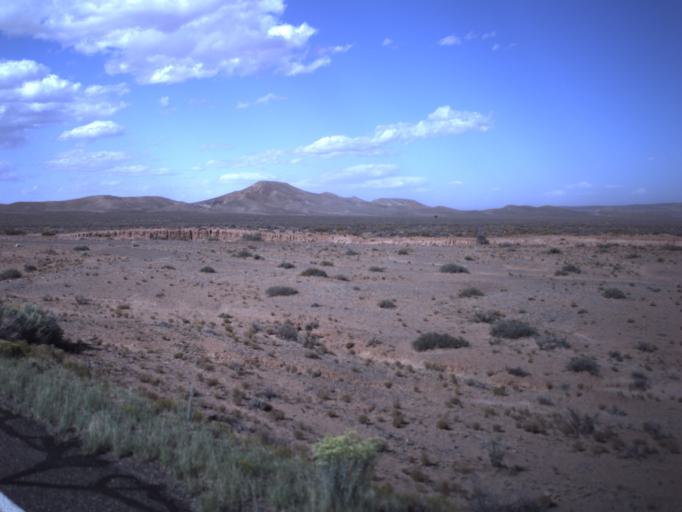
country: US
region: Utah
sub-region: Wayne County
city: Loa
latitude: 38.0985
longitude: -110.6223
